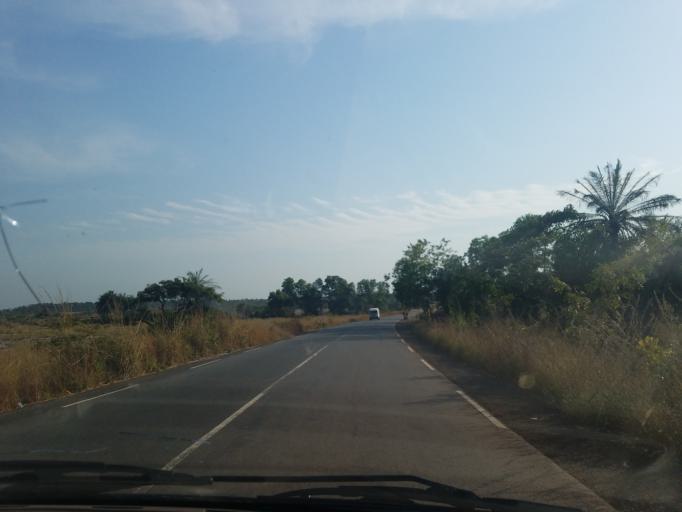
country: GN
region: Boke
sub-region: Boke Prefecture
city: Sangueya
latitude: 10.5007
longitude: -14.4050
